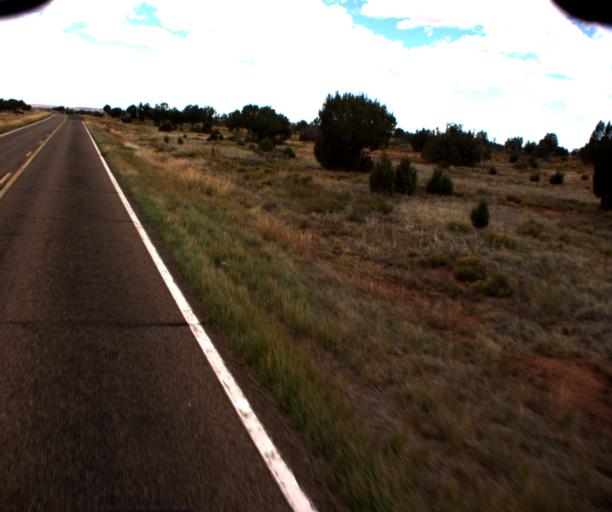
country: US
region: Arizona
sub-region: Navajo County
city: Heber-Overgaard
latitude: 34.5380
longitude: -110.4215
